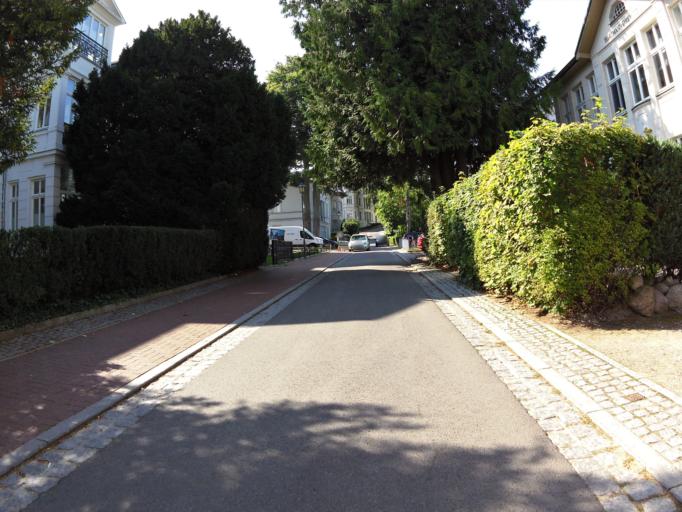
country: DE
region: Mecklenburg-Vorpommern
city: Seebad Heringsdorf
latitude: 53.9573
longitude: 14.1653
